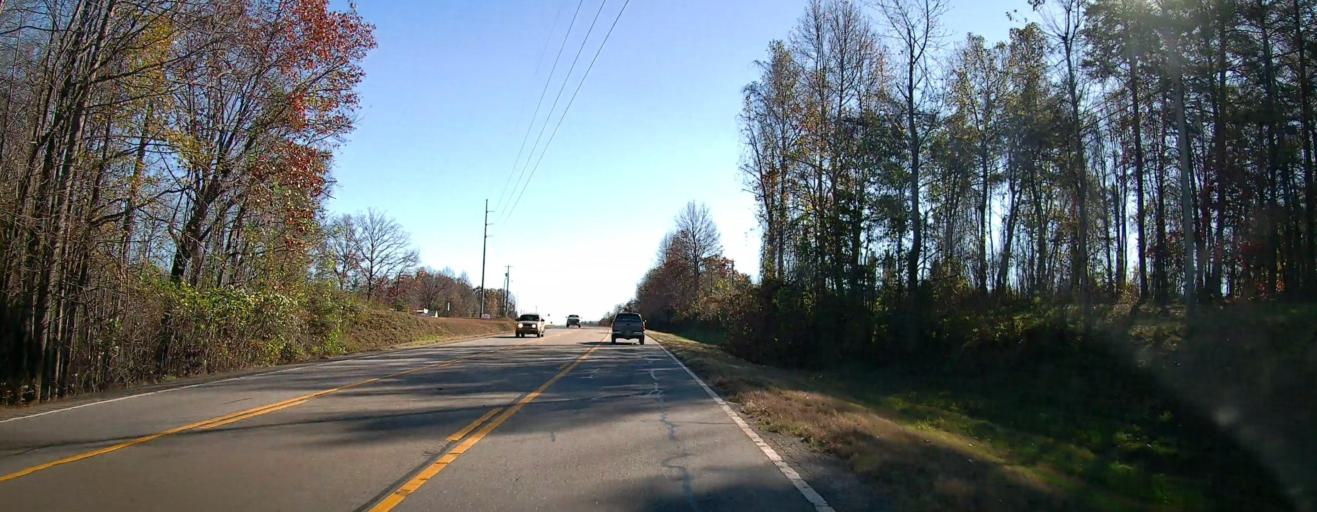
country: US
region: Georgia
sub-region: White County
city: Cleveland
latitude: 34.5473
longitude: -83.7607
